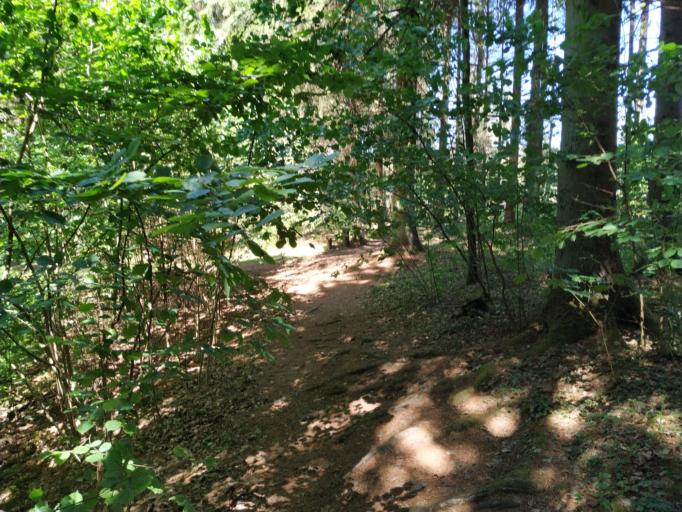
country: LT
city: Grigiskes
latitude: 54.8096
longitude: 25.0047
